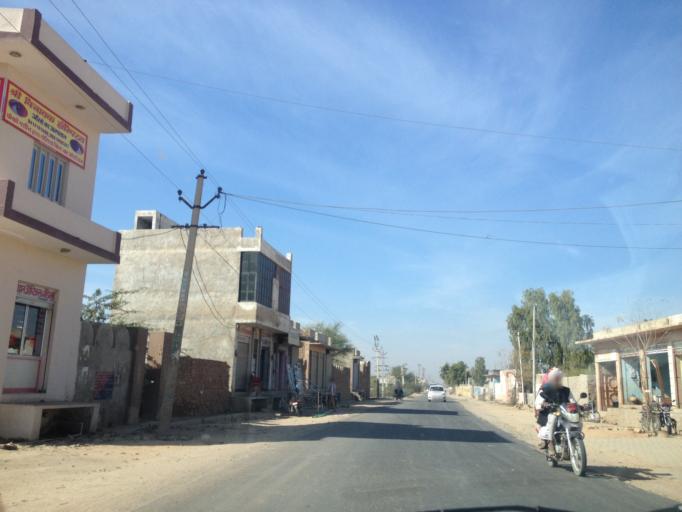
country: IN
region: Rajasthan
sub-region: Nagaur
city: Merta
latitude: 26.6443
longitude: 74.0253
